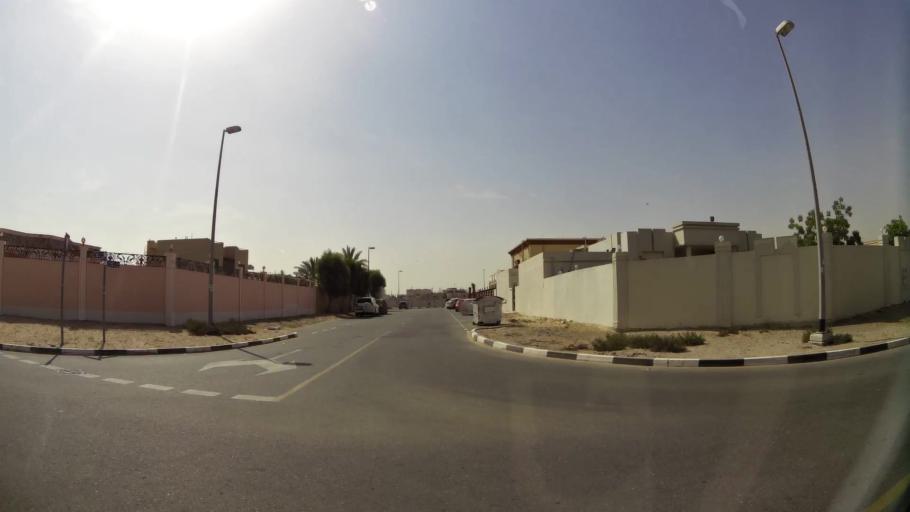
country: AE
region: Ash Shariqah
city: Sharjah
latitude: 25.2750
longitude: 55.4022
